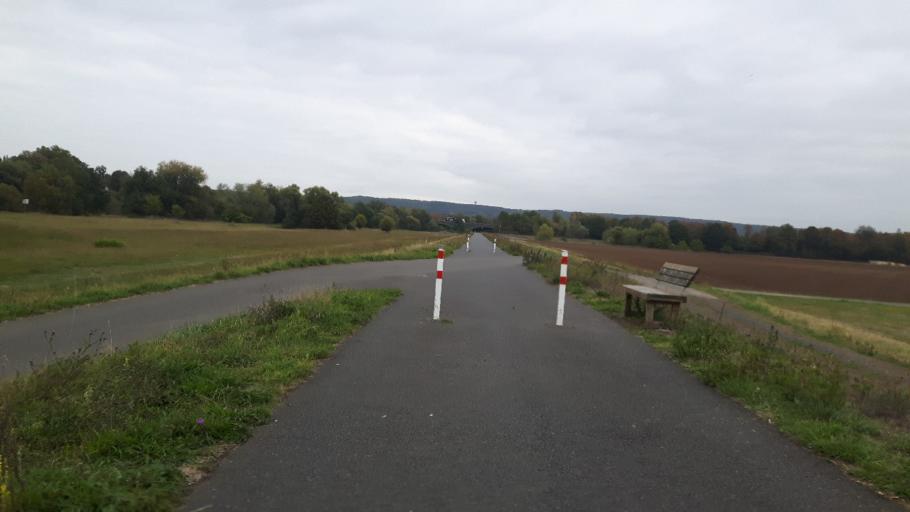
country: DE
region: North Rhine-Westphalia
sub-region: Regierungsbezirk Koln
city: Stossdorf
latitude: 50.7880
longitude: 7.2288
